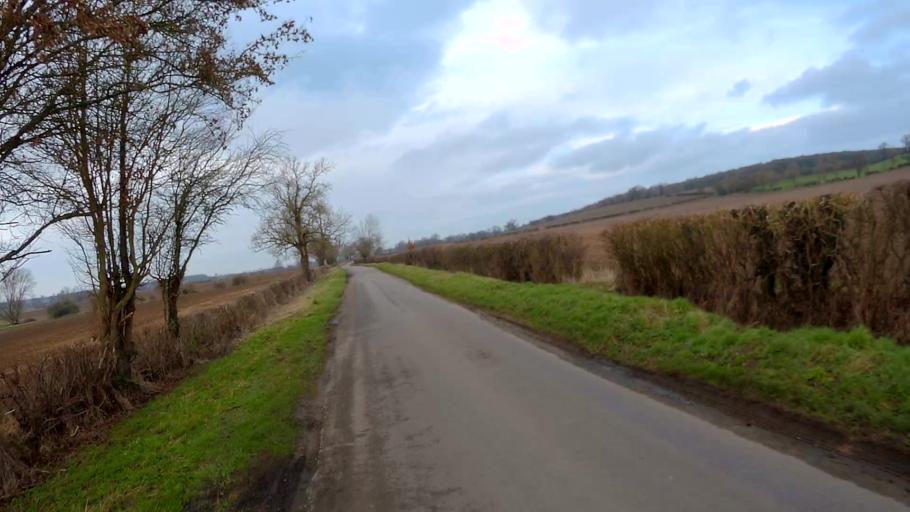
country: GB
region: England
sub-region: Lincolnshire
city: Bourne
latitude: 52.7876
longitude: -0.4254
